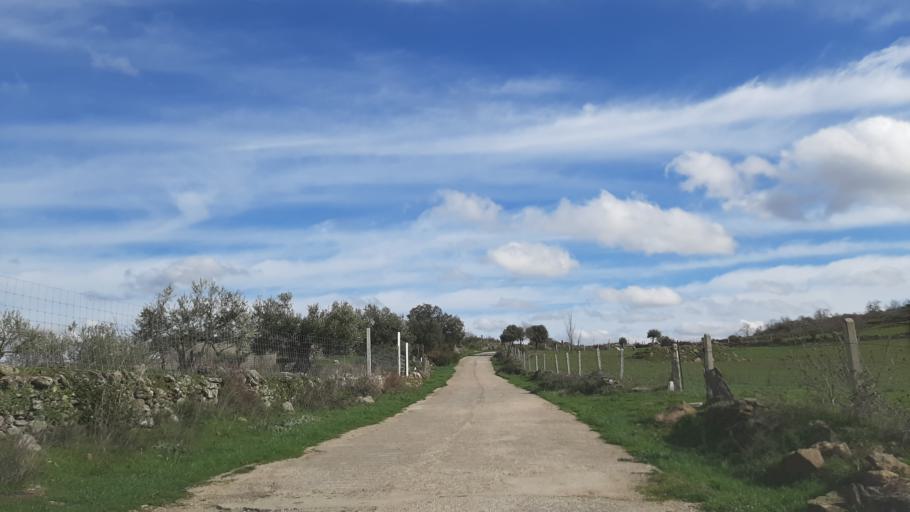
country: ES
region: Castille and Leon
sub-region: Provincia de Salamanca
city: Villarino de los Aires
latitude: 41.2536
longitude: -6.5254
